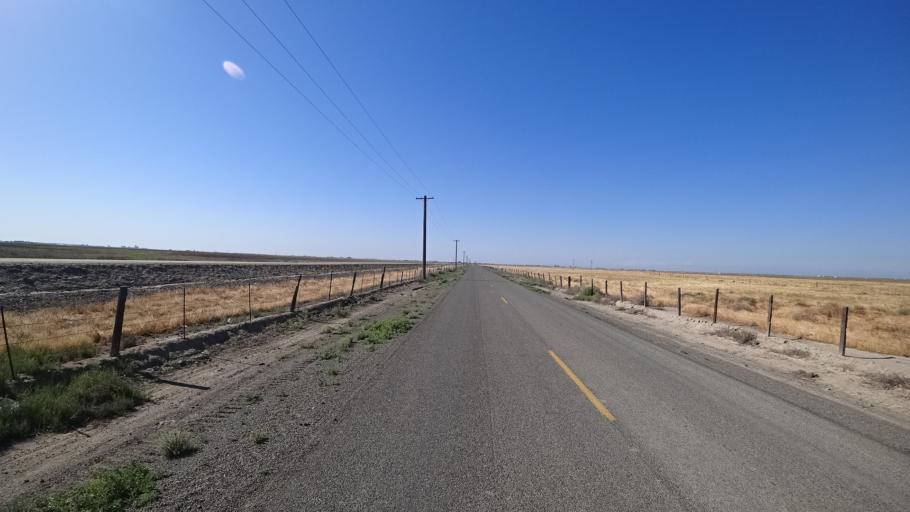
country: US
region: California
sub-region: Kings County
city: Corcoran
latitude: 36.1614
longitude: -119.5648
